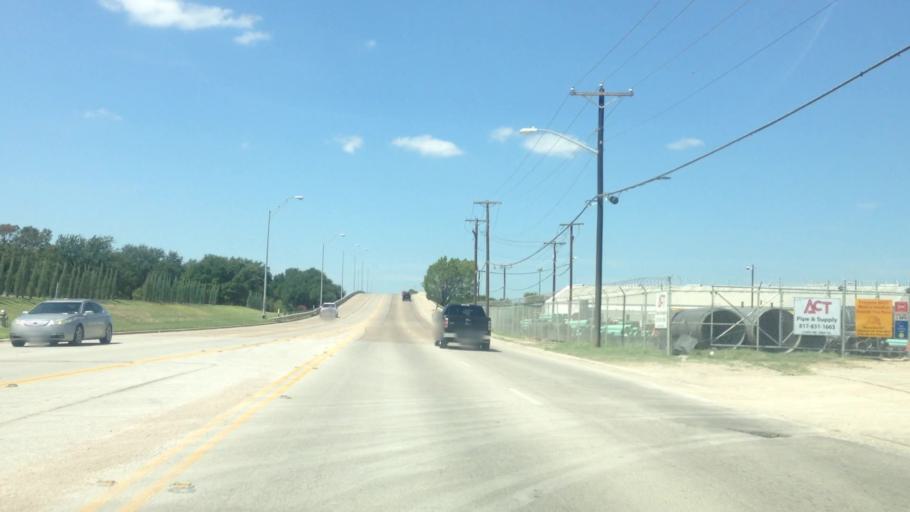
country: US
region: Texas
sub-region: Tarrant County
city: Haltom City
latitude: 32.7952
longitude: -97.3117
